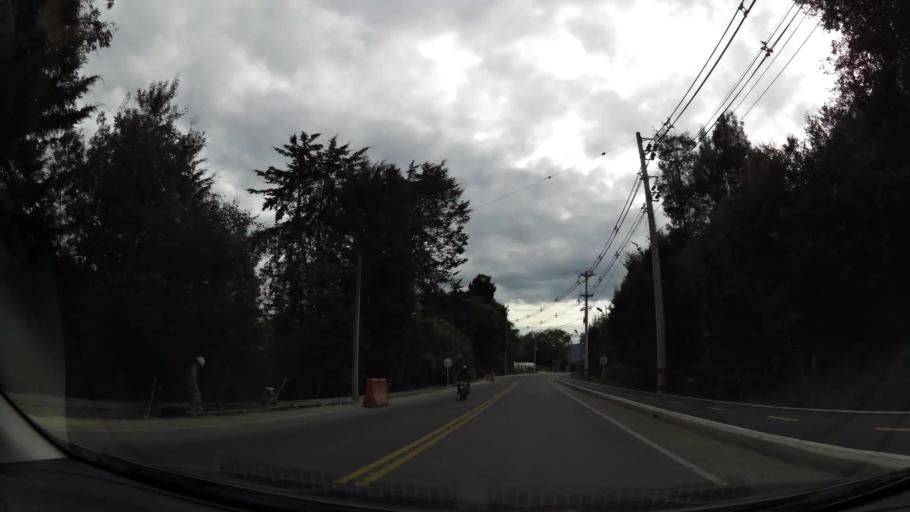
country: CO
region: Antioquia
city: Rionegro
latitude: 6.1488
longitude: -75.4195
